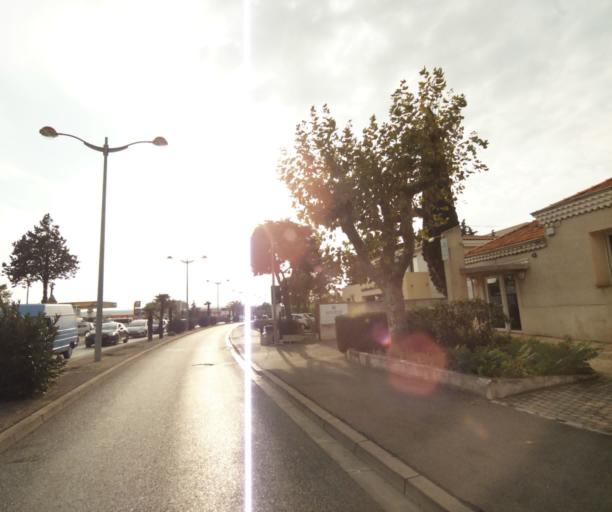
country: FR
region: Provence-Alpes-Cote d'Azur
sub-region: Departement des Bouches-du-Rhone
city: Marignane
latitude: 43.4117
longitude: 5.2185
